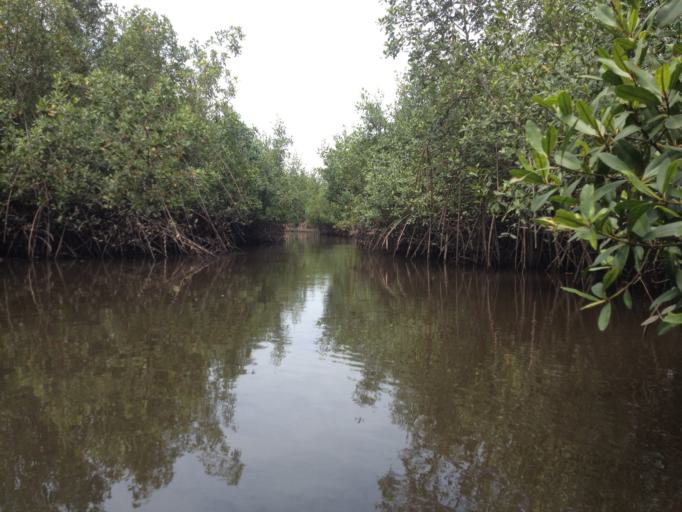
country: BJ
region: Mono
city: Grand-Popo
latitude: 6.3131
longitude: 1.9133
